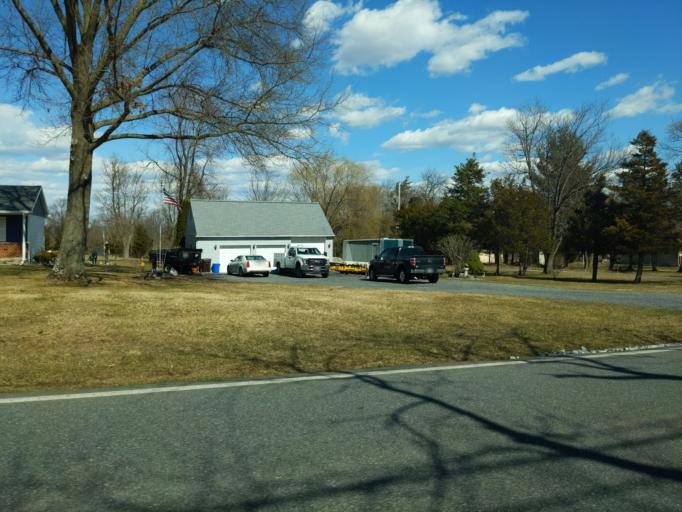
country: US
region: Pennsylvania
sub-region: Montgomery County
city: Red Hill
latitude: 40.3479
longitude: -75.5148
